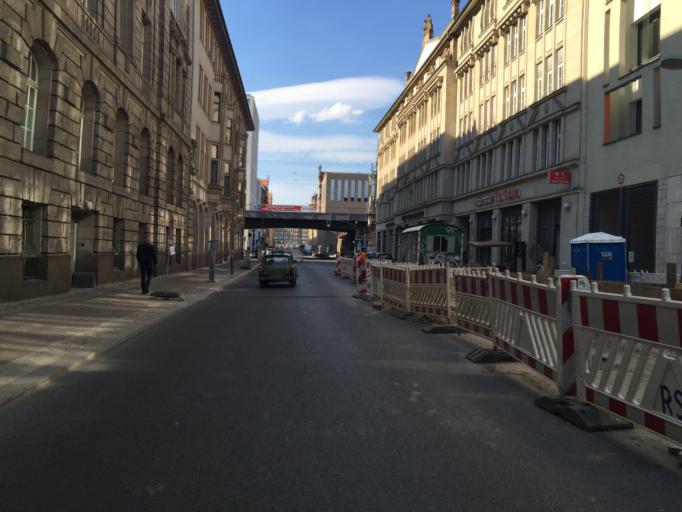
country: DE
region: Berlin
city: Mitte
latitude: 52.5192
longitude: 13.3922
